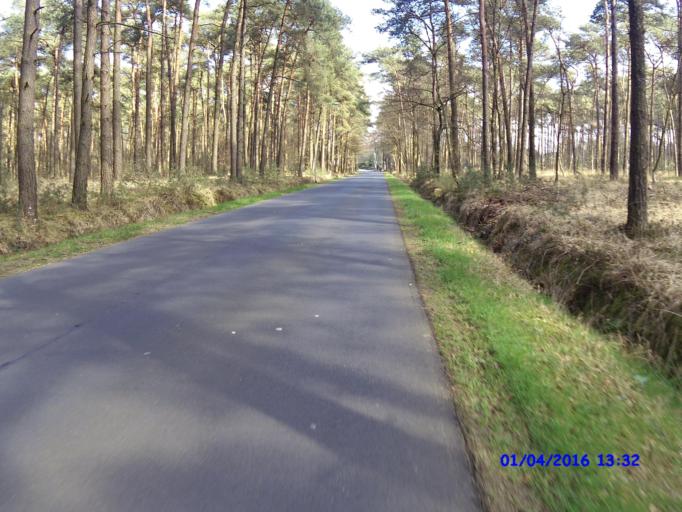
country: BE
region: Flanders
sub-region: Provincie Antwerpen
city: Brasschaat
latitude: 51.3107
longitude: 4.5506
